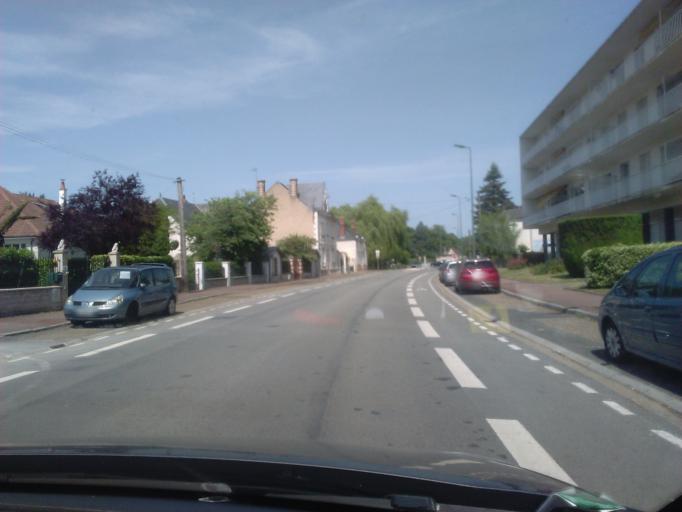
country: FR
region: Centre
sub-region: Departement du Loir-et-Cher
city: Vendome
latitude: 47.7962
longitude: 1.0563
